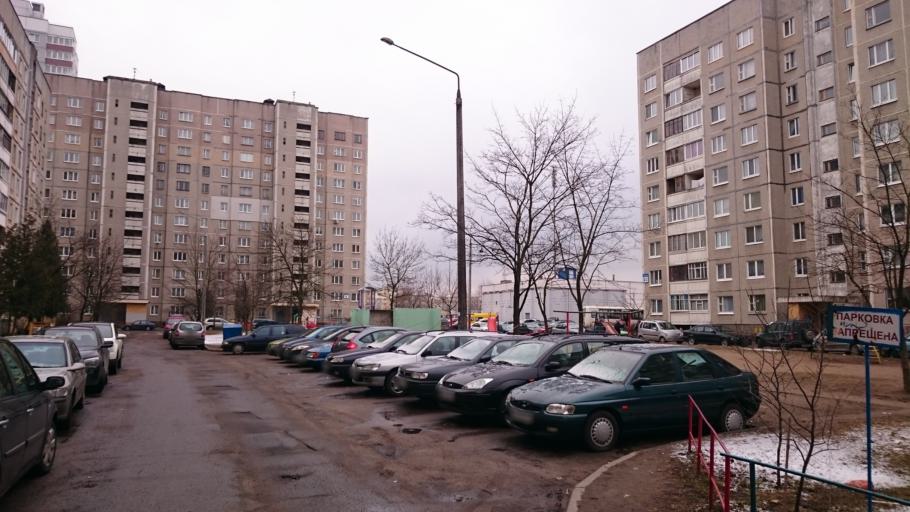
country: BY
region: Minsk
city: Borovlyany
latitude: 53.9373
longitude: 27.6861
